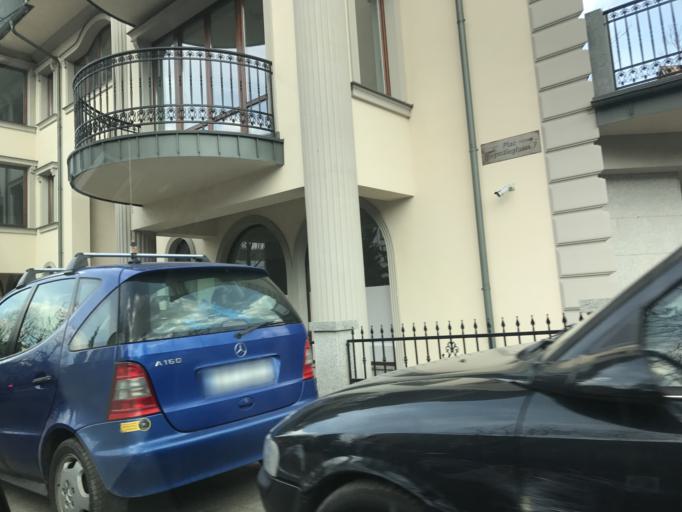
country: PL
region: Lesser Poland Voivodeship
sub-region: Powiat tatrzanski
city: Zakopane
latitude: 49.2921
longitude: 19.9536
